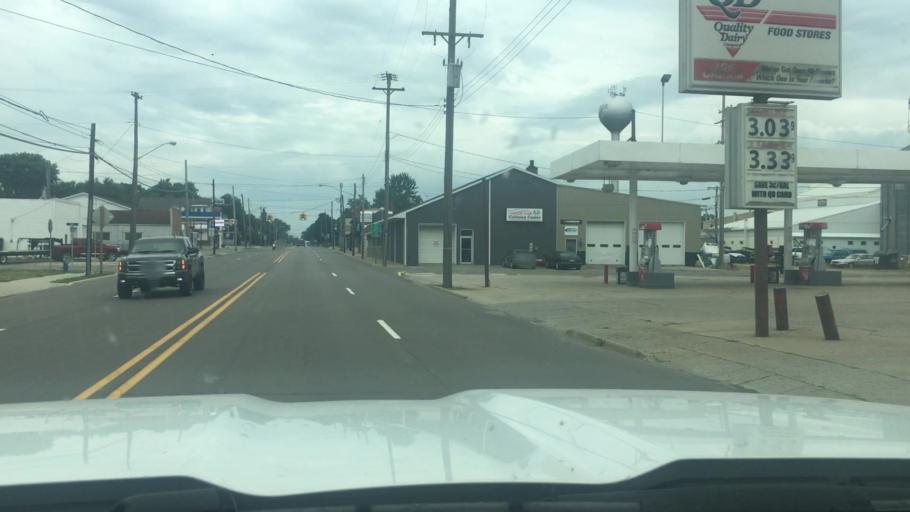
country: US
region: Michigan
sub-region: Clinton County
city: Fowler
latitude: 43.0019
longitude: -84.7378
